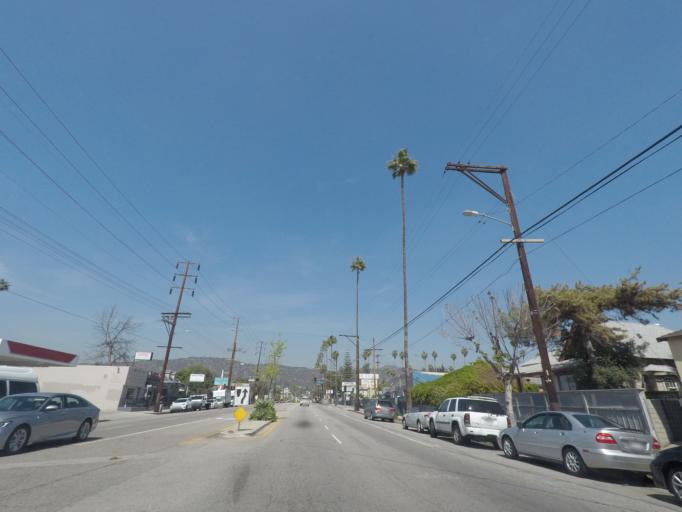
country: US
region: California
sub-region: Los Angeles County
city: Glendale
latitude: 34.1315
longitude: -118.2163
